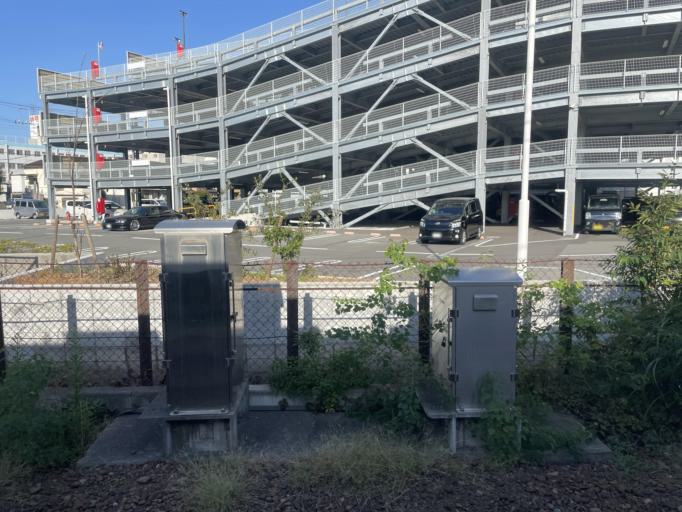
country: JP
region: Osaka
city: Osaka-shi
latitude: 34.6467
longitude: 135.4836
